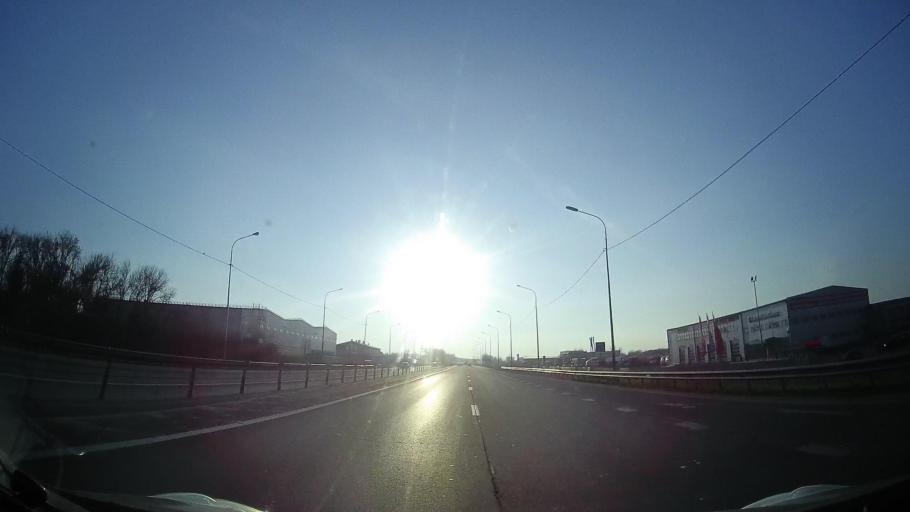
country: RU
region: Rostov
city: Ol'ginskaya
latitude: 47.1214
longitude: 39.8644
